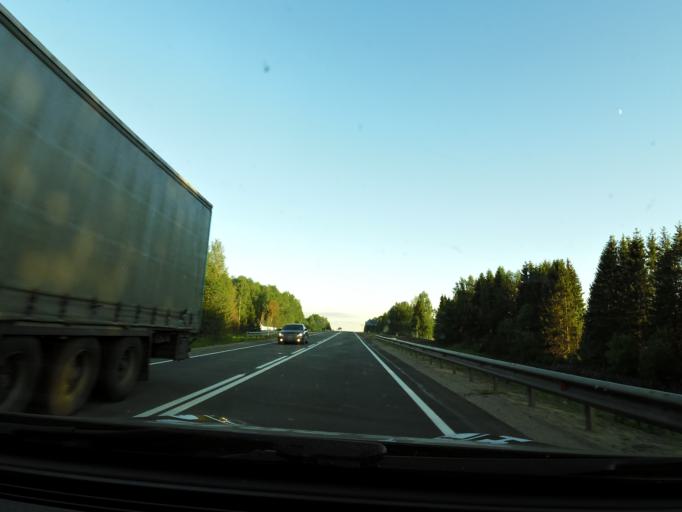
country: RU
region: Vologda
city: Gryazovets
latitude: 58.7192
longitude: 40.2964
